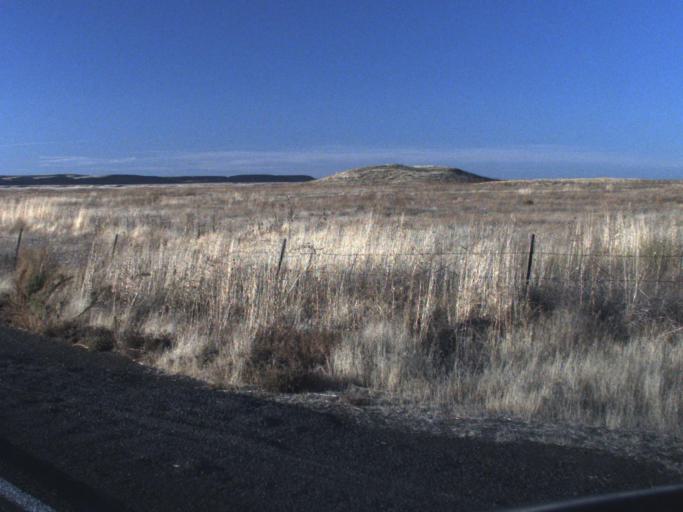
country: US
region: Washington
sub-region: Walla Walla County
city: Waitsburg
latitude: 46.6562
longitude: -118.2644
